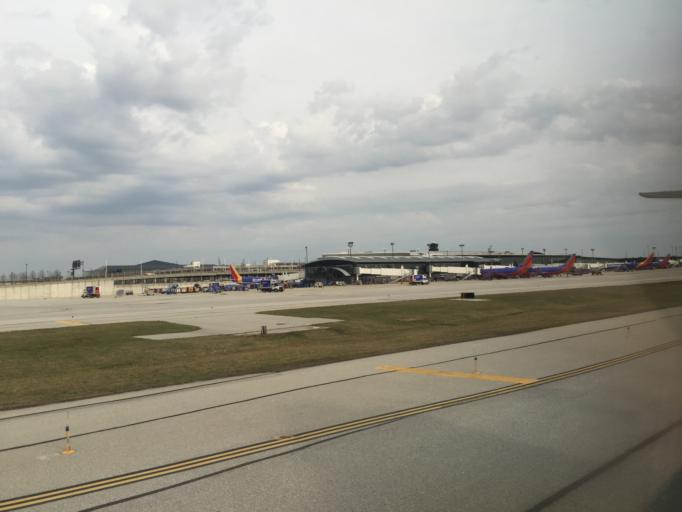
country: US
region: Maryland
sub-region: Anne Arundel County
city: Linthicum
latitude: 39.1809
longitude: -76.6762
